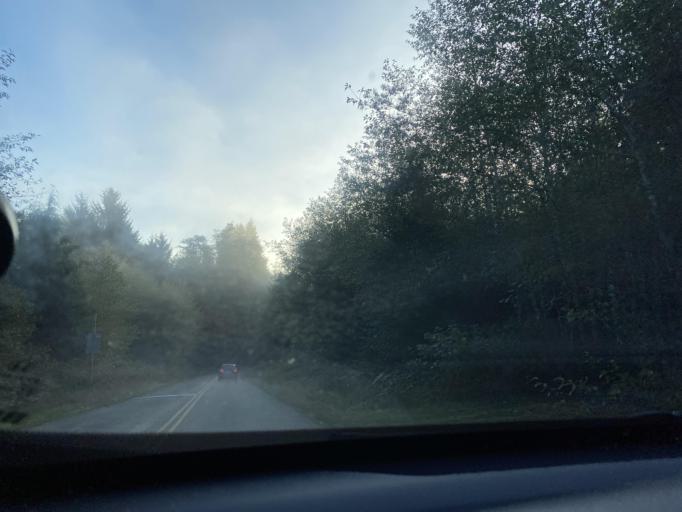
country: US
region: Washington
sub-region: Clallam County
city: Forks
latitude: 47.8144
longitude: -124.0676
